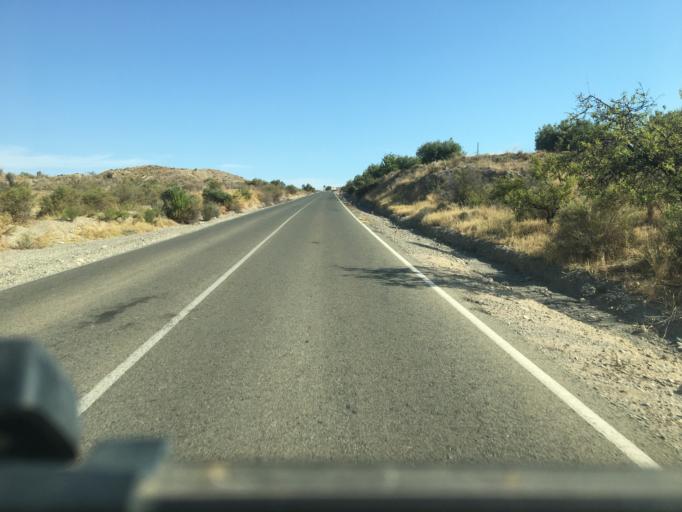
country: ES
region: Andalusia
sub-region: Provincia de Almeria
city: Huercal-Overa
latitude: 37.4243
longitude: -1.9707
